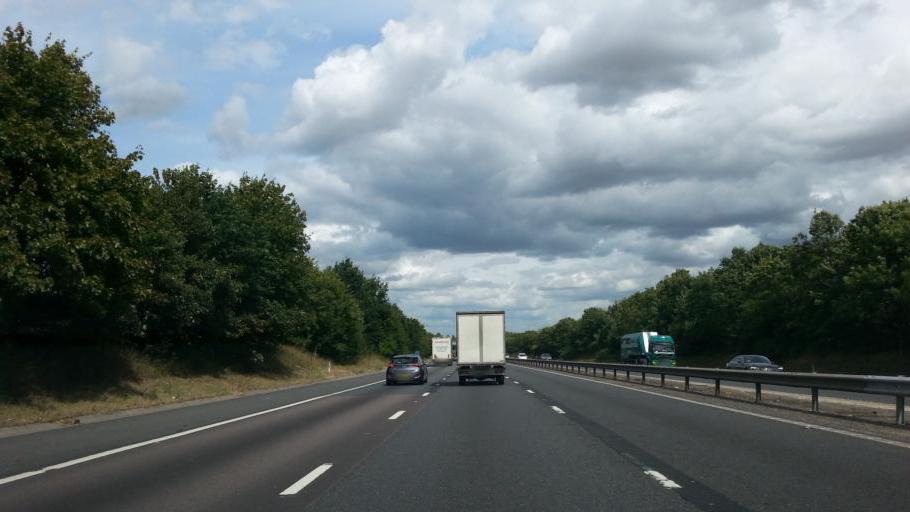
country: GB
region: England
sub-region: Essex
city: Harlow
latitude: 51.7680
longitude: 0.1556
